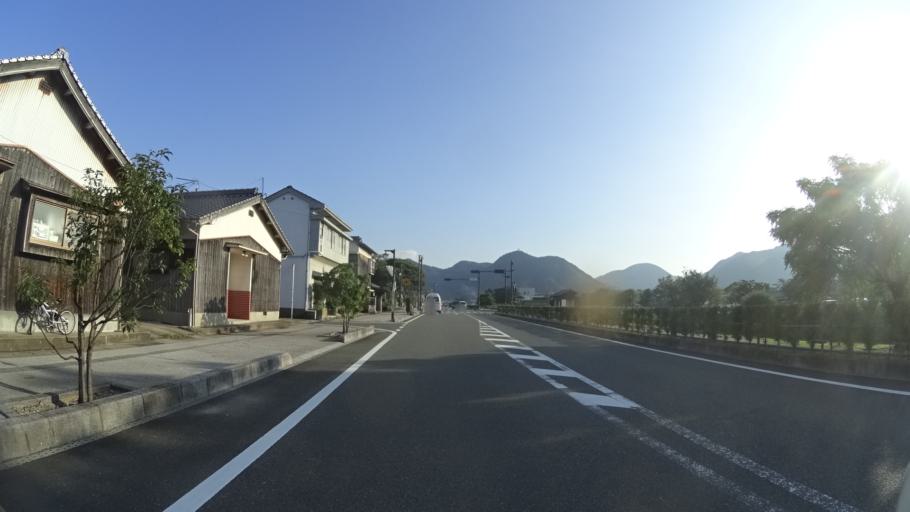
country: JP
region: Yamaguchi
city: Hagi
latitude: 34.4139
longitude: 131.3924
